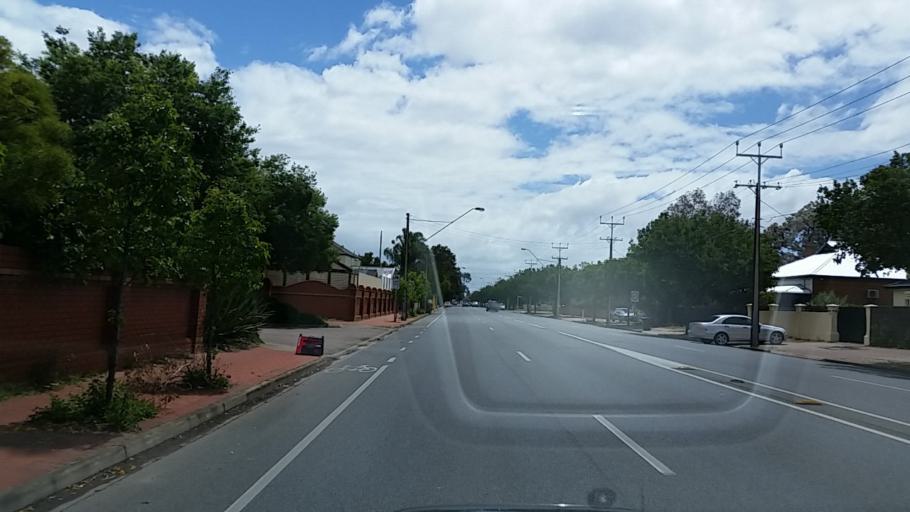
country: AU
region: South Australia
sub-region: Prospect
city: Prospect
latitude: -34.8921
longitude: 138.5761
